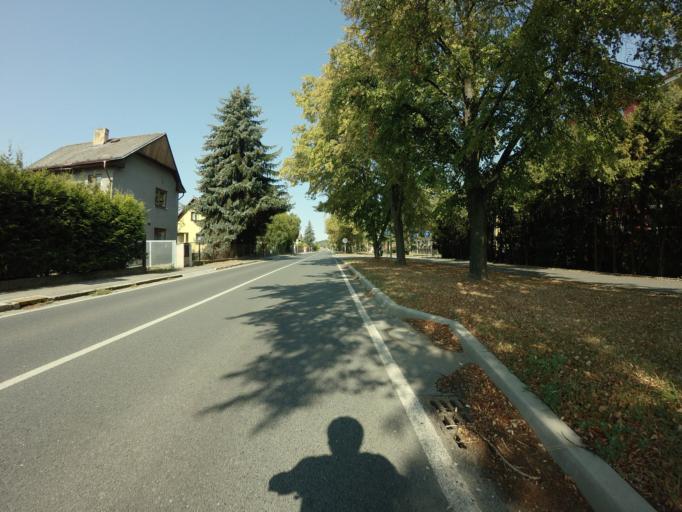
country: CZ
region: Central Bohemia
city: Tynec nad Sazavou
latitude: 49.8354
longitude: 14.5868
